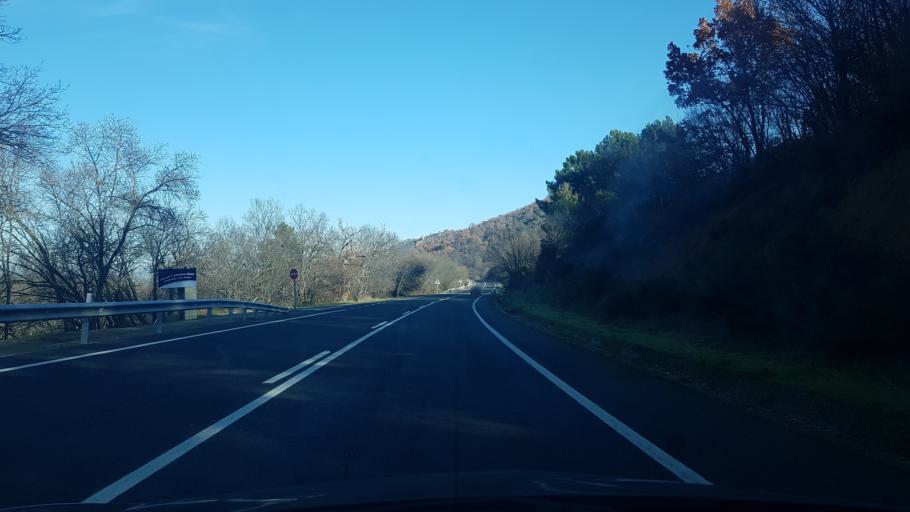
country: ES
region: Castille and Leon
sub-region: Provincia de Avila
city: Navahondilla
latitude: 40.3120
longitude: -4.5080
